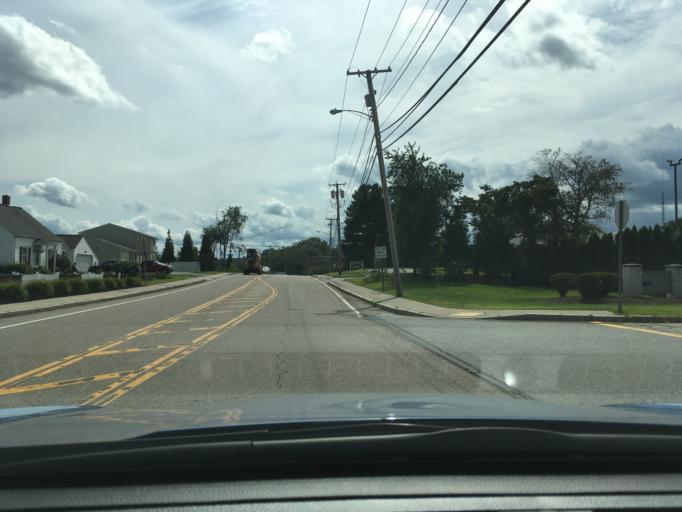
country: US
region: Rhode Island
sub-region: Providence County
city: Johnston
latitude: 41.8309
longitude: -71.4987
